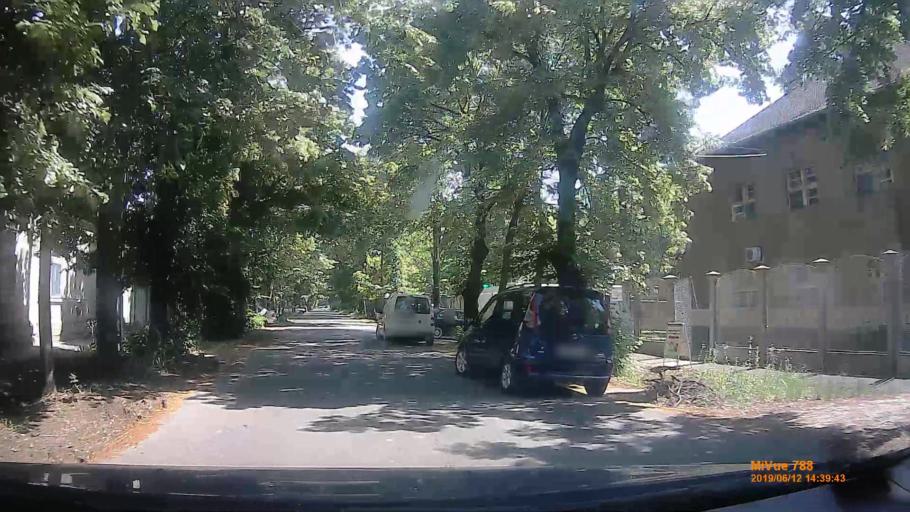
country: HU
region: Csongrad
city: Mako
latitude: 46.2088
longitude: 20.4705
